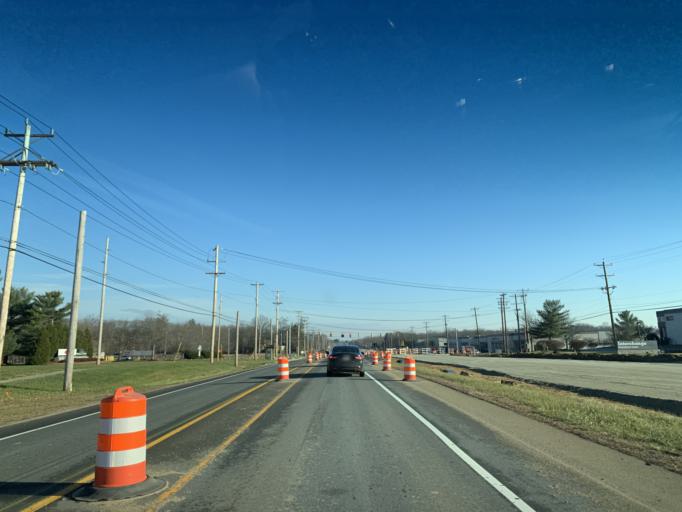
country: US
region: Delaware
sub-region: New Castle County
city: Newark
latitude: 39.6600
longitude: -75.7824
